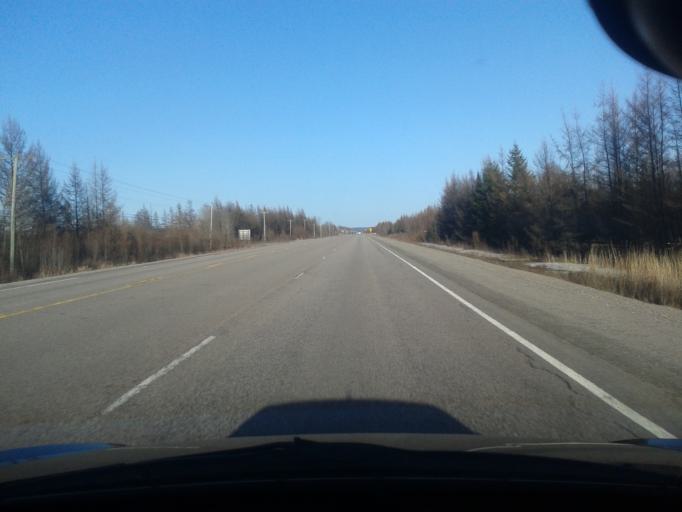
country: CA
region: Ontario
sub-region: Nipissing District
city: North Bay
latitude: 46.3672
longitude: -79.8198
